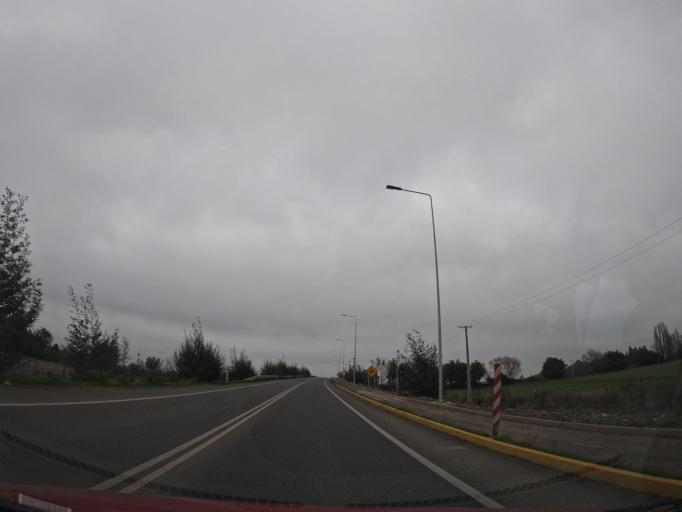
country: CL
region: Maule
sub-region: Provincia de Talca
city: San Clemente
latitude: -35.5146
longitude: -71.5008
